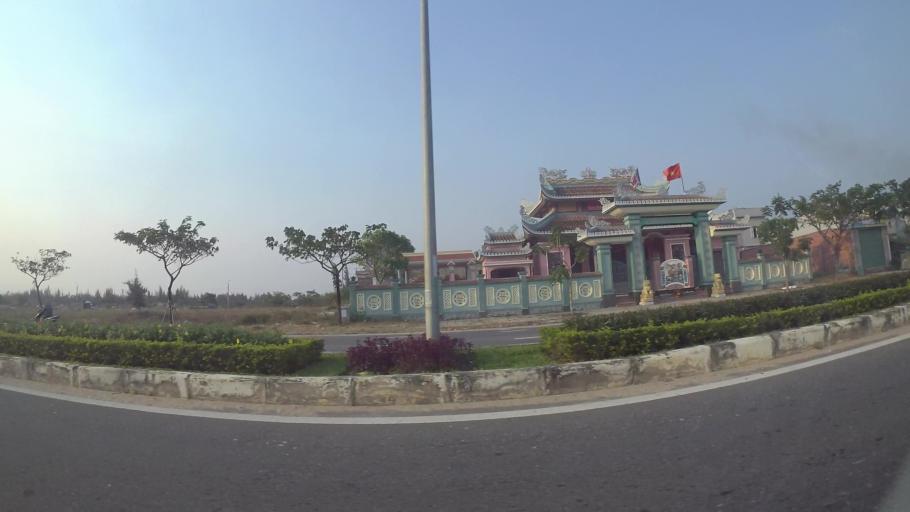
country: VN
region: Da Nang
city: Ngu Hanh Son
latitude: 15.9831
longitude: 108.2475
